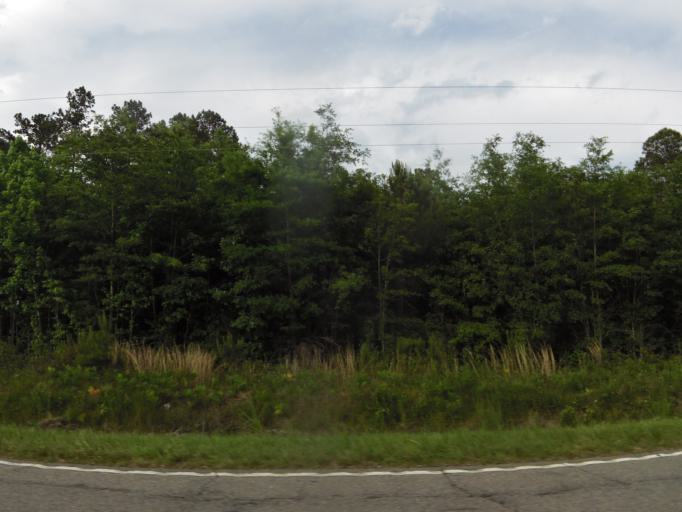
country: US
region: South Carolina
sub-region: Jasper County
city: Ridgeland
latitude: 32.4924
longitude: -81.1258
